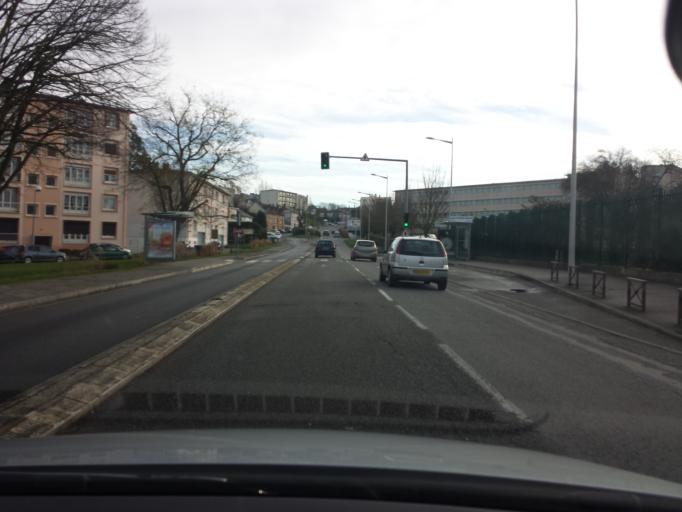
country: FR
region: Haute-Normandie
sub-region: Departement de l'Eure
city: Evreux
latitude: 49.0184
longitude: 1.1559
